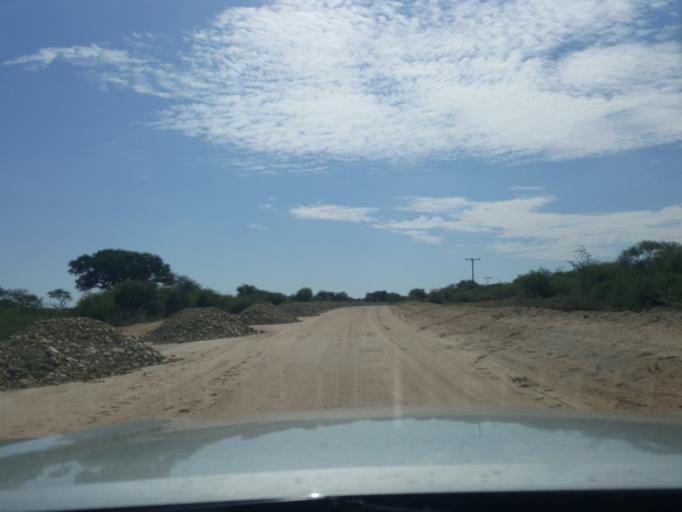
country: BW
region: Kweneng
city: Letlhakeng
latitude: -24.0438
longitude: 25.0141
